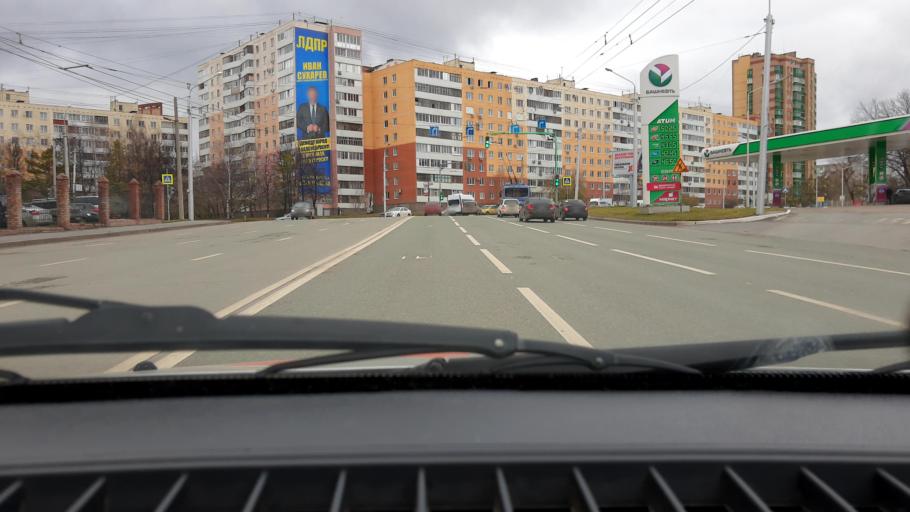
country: RU
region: Bashkortostan
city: Ufa
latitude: 54.7616
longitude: 56.0228
